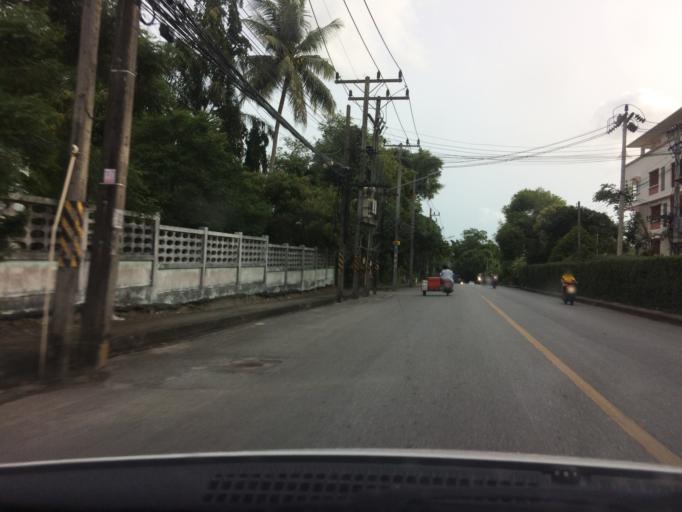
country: TH
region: Phuket
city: Ban Talat Yai
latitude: 7.8896
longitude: 98.4058
